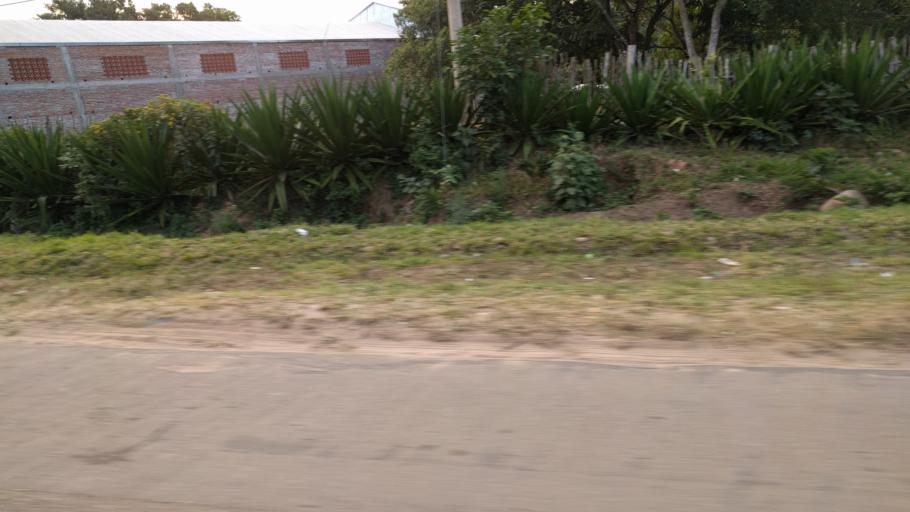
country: BO
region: Santa Cruz
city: Buena Vista
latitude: -17.4548
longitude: -63.6565
